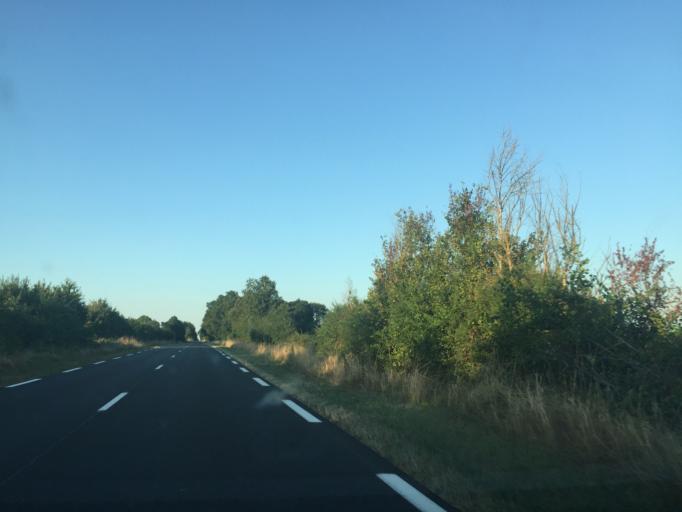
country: FR
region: Poitou-Charentes
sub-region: Departement de la Vienne
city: Lusignan
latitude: 46.4128
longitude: 0.0920
